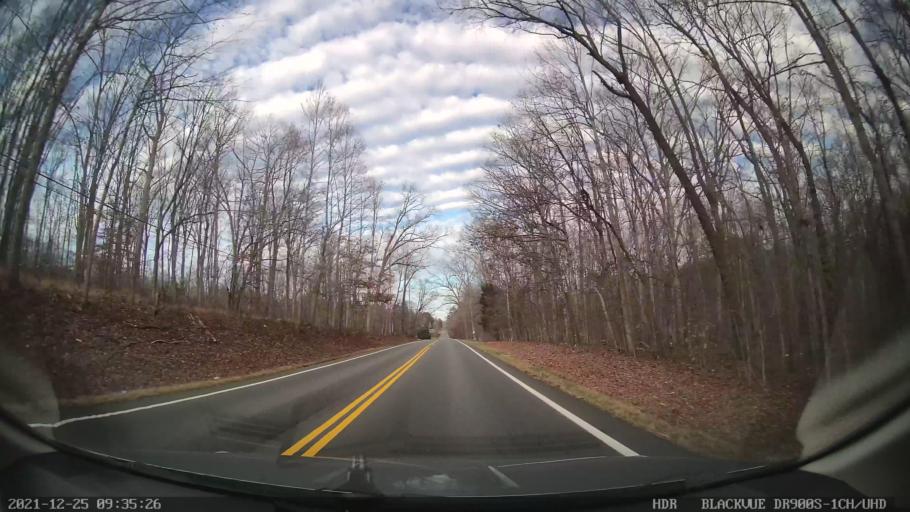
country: US
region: Virginia
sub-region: Goochland County
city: Goochland
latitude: 37.7622
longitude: -77.8769
